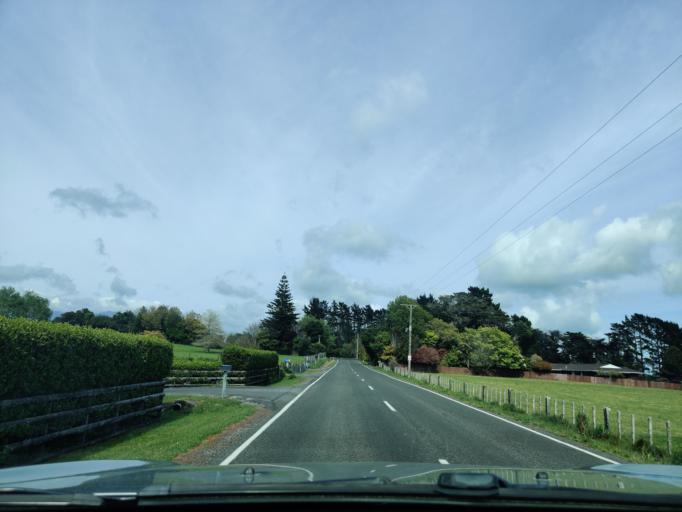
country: NZ
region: Taranaki
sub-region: New Plymouth District
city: New Plymouth
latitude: -39.1159
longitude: 174.0967
